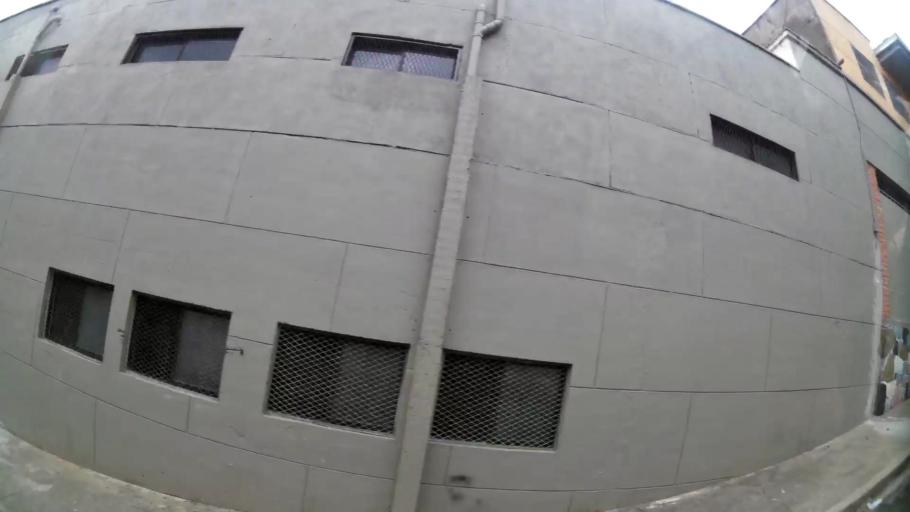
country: CO
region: Antioquia
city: Medellin
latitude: 6.2362
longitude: -75.5499
